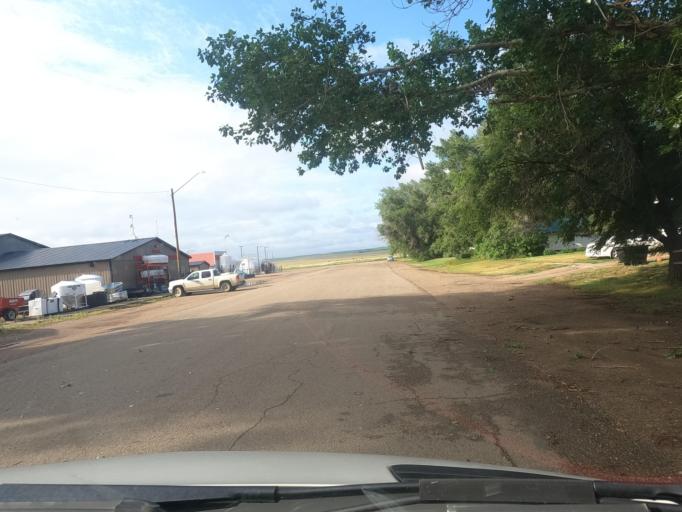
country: CA
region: Saskatchewan
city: Gravelbourg
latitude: 49.6870
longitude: -107.1377
